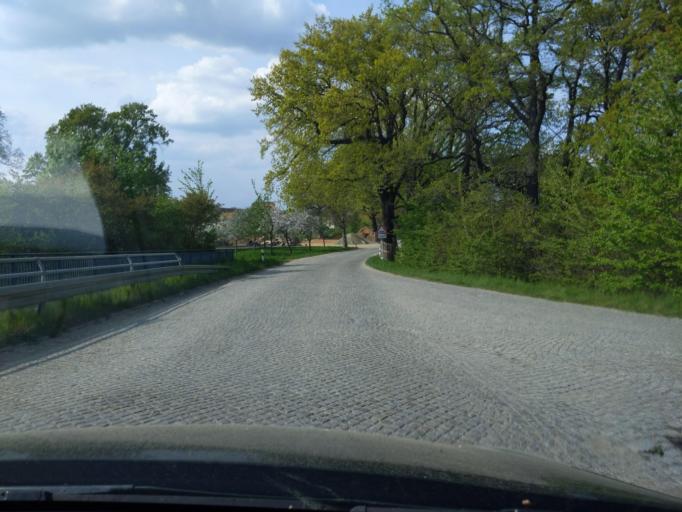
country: DE
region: Saxony
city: Malschwitz
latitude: 51.2080
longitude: 14.5304
